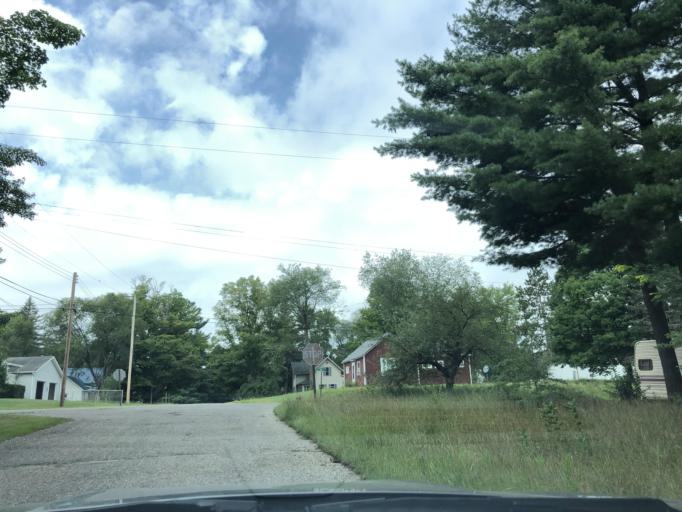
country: US
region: Michigan
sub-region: Osceola County
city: Evart
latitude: 44.1008
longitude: -85.1508
